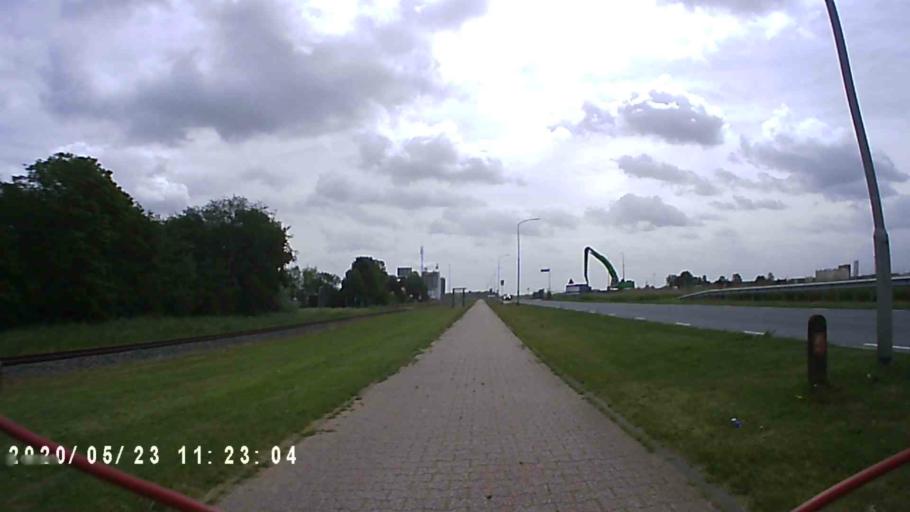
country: NL
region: Groningen
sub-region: Gemeente Delfzijl
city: Delfzijl
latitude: 53.3038
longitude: 6.9800
